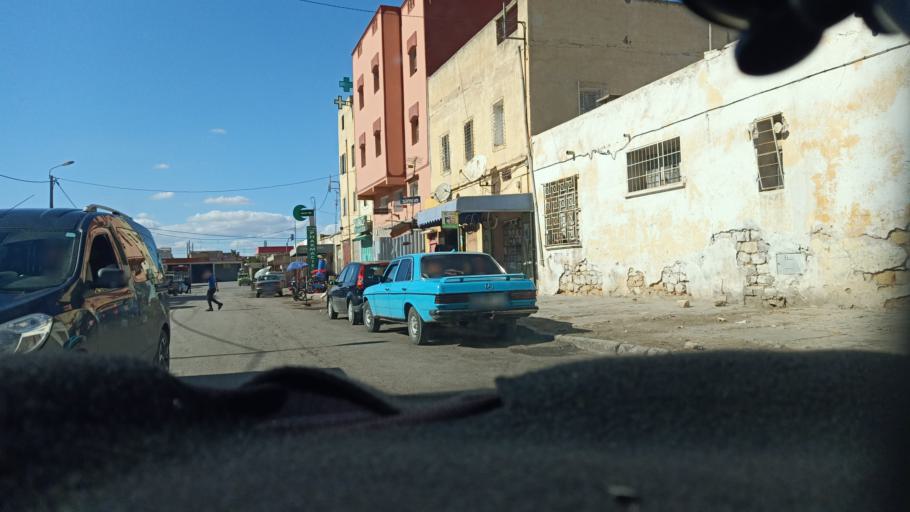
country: MA
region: Doukkala-Abda
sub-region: Safi
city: Youssoufia
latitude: 32.2413
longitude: -8.5368
